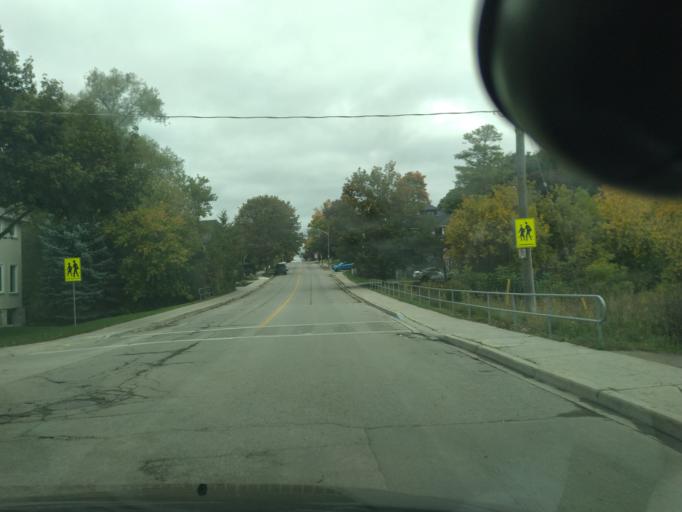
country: CA
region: Ontario
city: Newmarket
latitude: 44.0501
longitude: -79.4632
